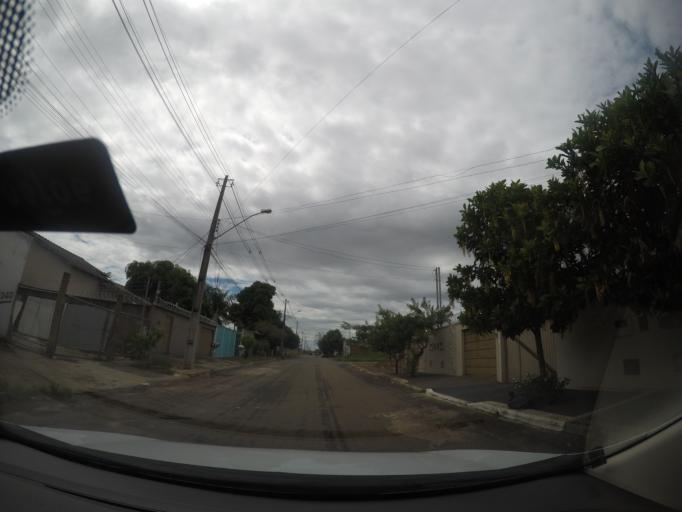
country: BR
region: Goias
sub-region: Goiania
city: Goiania
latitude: -16.7234
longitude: -49.3501
